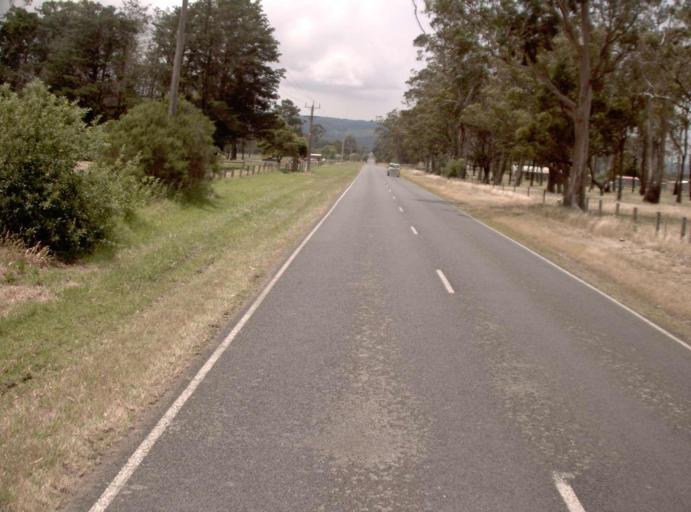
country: AU
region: Victoria
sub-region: Latrobe
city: Traralgon
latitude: -38.5345
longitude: 146.6579
